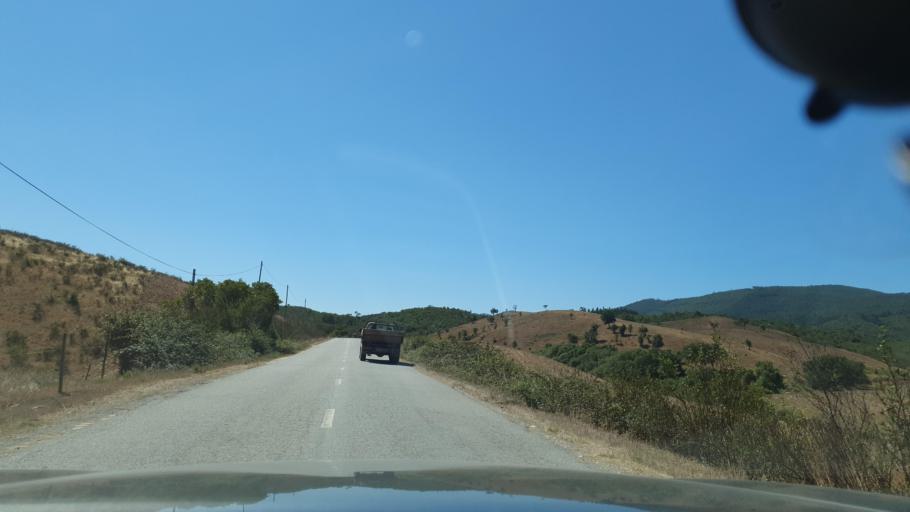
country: PT
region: Beja
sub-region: Odemira
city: Sao Teotonio
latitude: 37.4740
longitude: -8.6237
